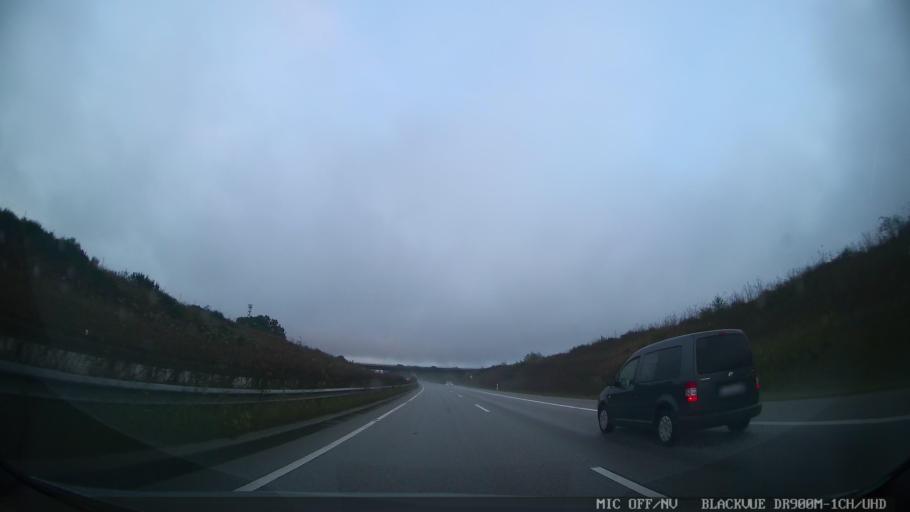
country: DE
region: Schleswig-Holstein
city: Badendorf
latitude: 53.8660
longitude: 10.5632
